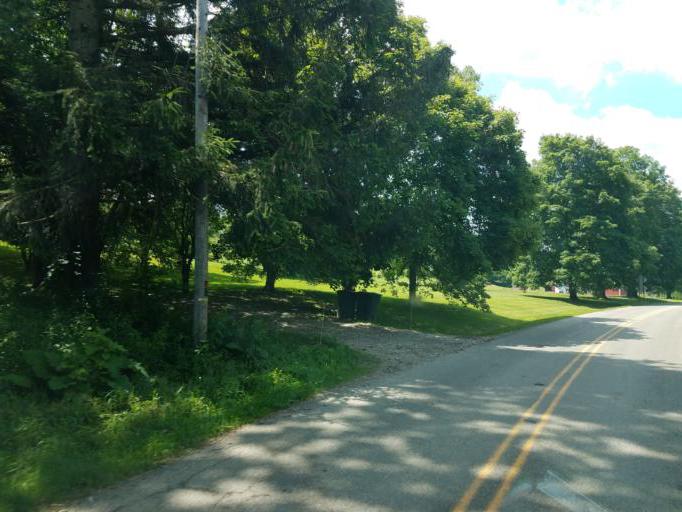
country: US
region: Ohio
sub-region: Knox County
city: Danville
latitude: 40.4558
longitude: -82.2866
